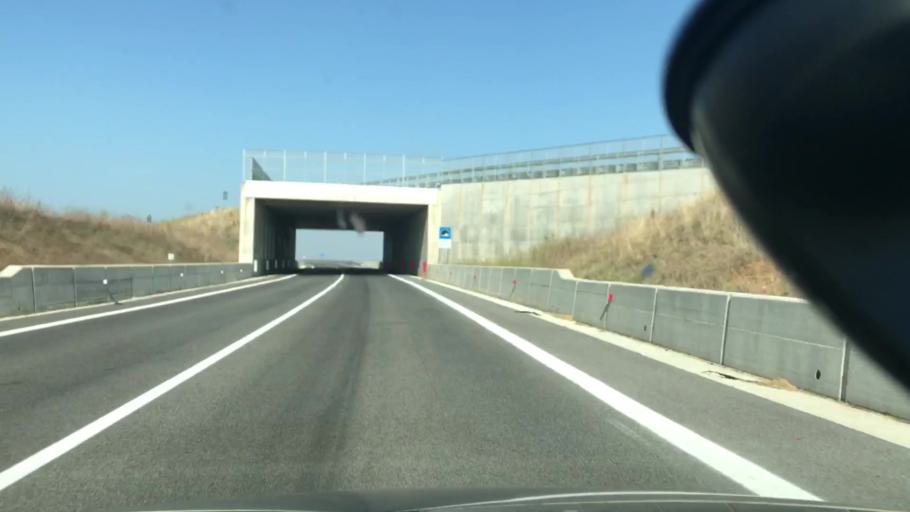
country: IT
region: Basilicate
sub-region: Provincia di Potenza
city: Palazzo San Gervasio
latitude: 40.9689
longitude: 16.0031
